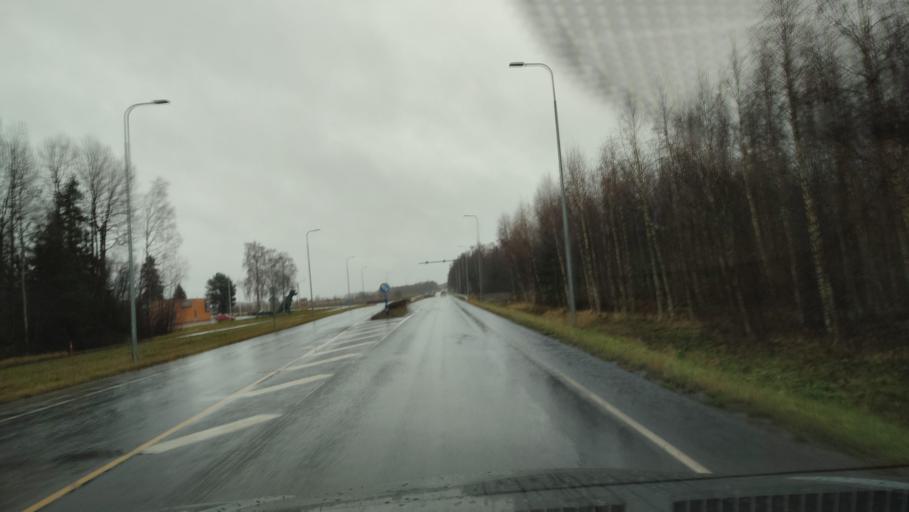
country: FI
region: Ostrobothnia
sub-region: Vaasa
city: Ristinummi
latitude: 63.0496
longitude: 21.7270
